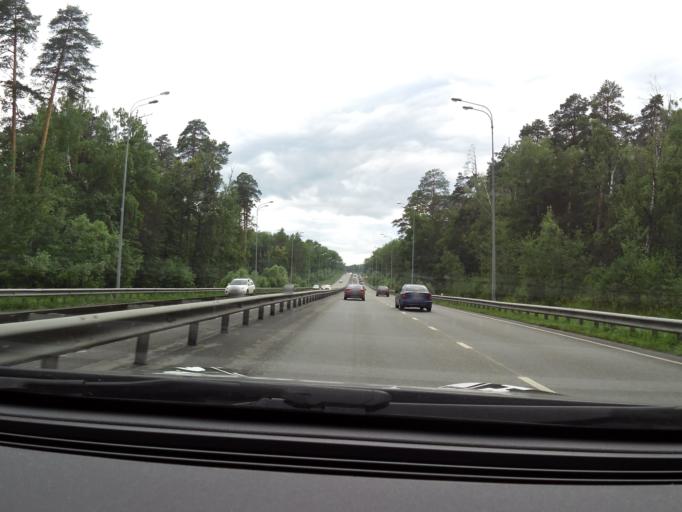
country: RU
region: Tatarstan
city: Staroye Arakchino
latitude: 55.8427
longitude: 48.9414
